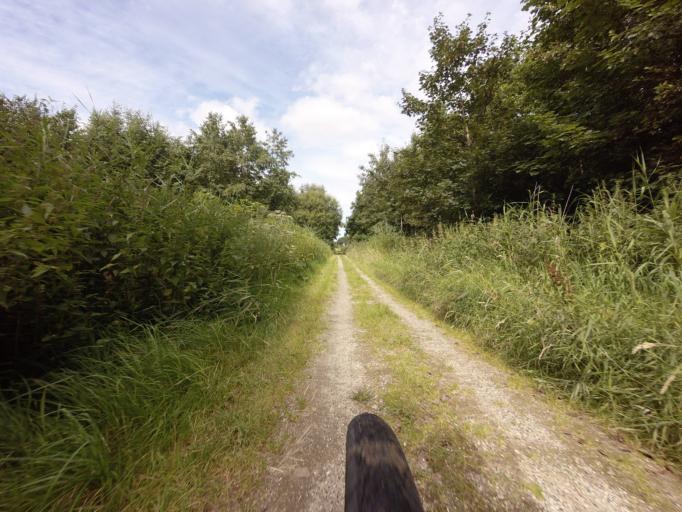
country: DK
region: Central Jutland
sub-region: Syddjurs Kommune
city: Ryomgard
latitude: 56.3880
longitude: 10.5329
